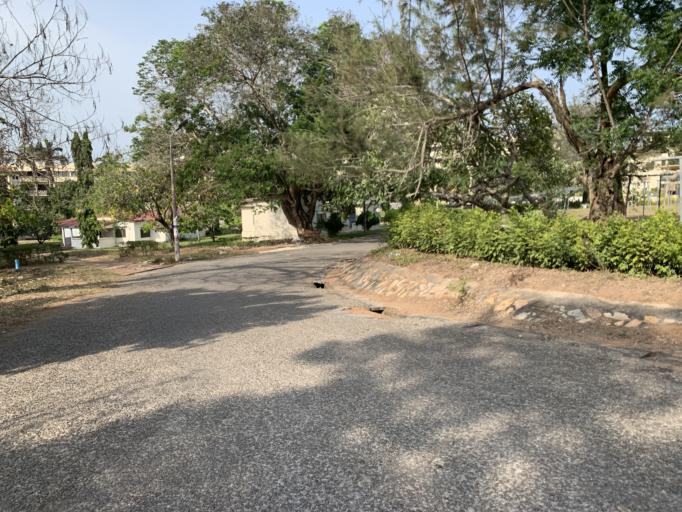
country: GH
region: Central
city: Winneba
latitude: 5.3379
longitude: -0.6264
